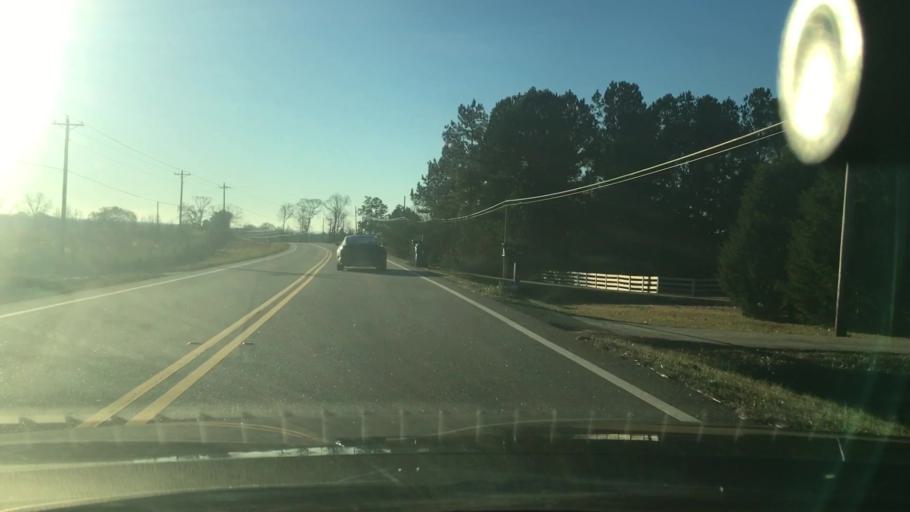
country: US
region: Georgia
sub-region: Coweta County
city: Senoia
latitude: 33.2776
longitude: -84.5341
